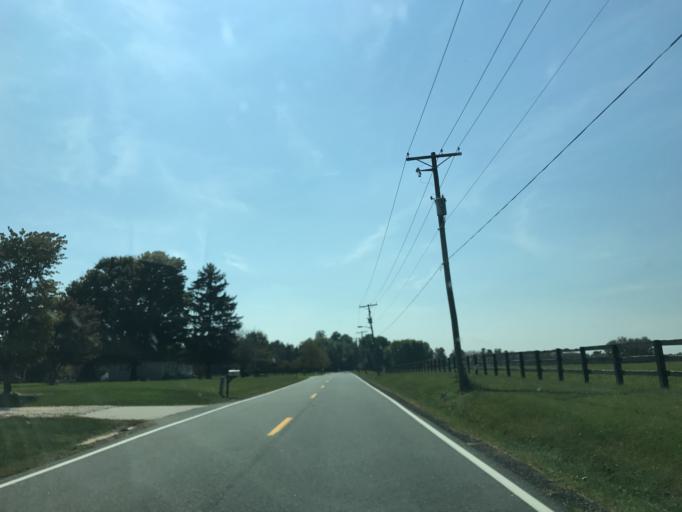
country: US
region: Delaware
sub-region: New Castle County
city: Middletown
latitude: 39.4984
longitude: -75.8066
